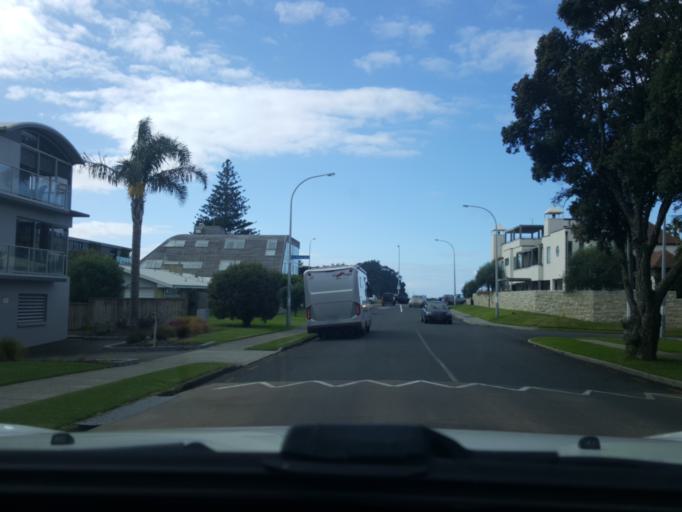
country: NZ
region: Bay of Plenty
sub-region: Tauranga City
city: Tauranga
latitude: -37.6377
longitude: 176.1868
